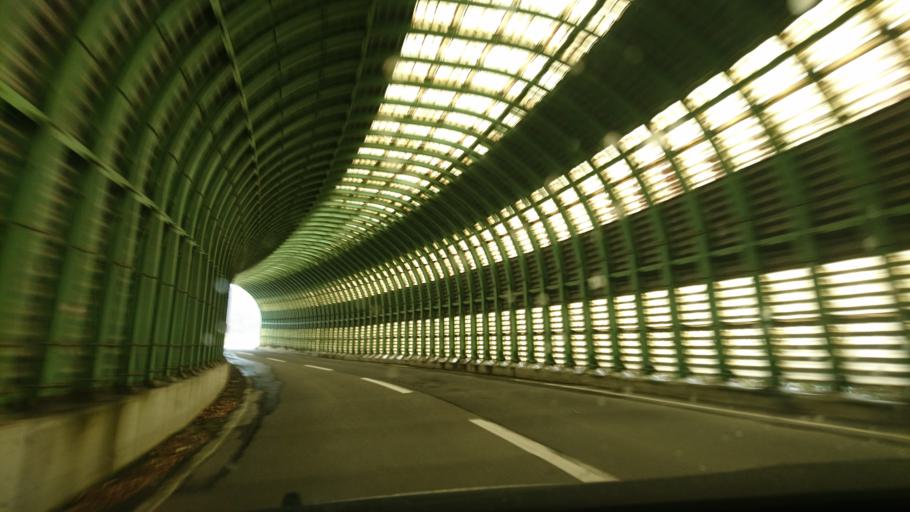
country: JP
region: Iwate
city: Ichinoseki
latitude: 38.9404
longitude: 140.8205
